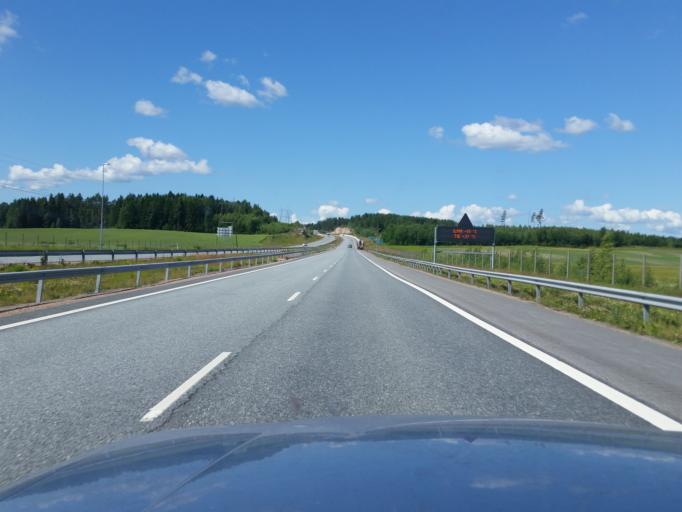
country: FI
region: Varsinais-Suomi
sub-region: Salo
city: Kiikala
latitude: 60.3907
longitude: 23.5755
